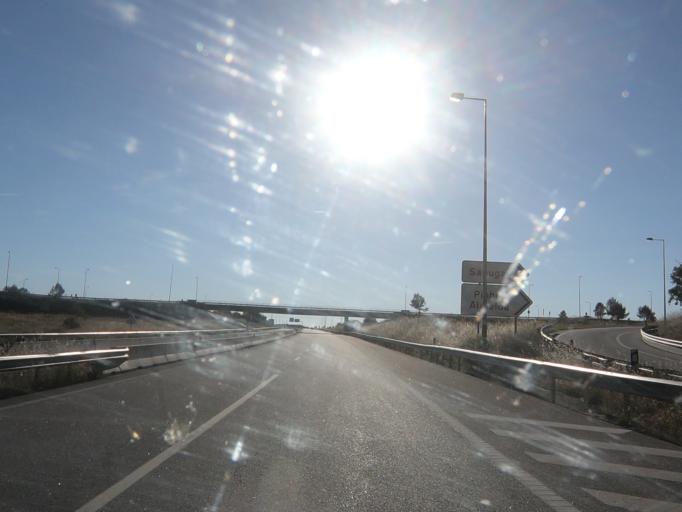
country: ES
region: Castille and Leon
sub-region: Provincia de Salamanca
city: Fuentes de Onoro
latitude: 40.6072
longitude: -6.9804
